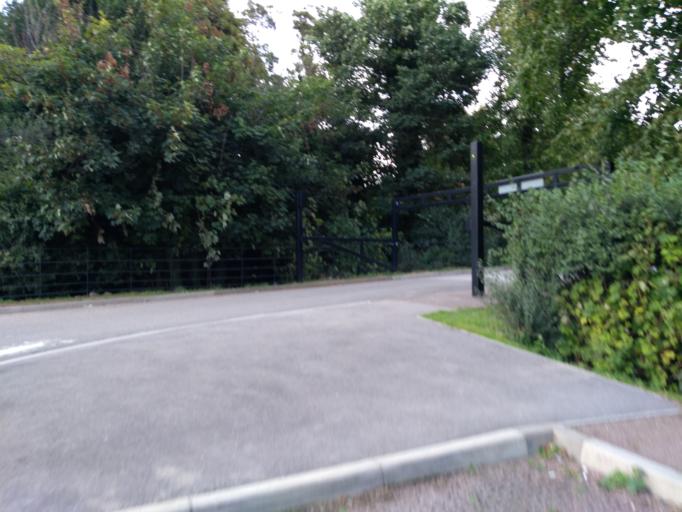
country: GB
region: England
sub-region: Central Bedfordshire
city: Houghton Regis
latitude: 51.9017
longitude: -0.5091
